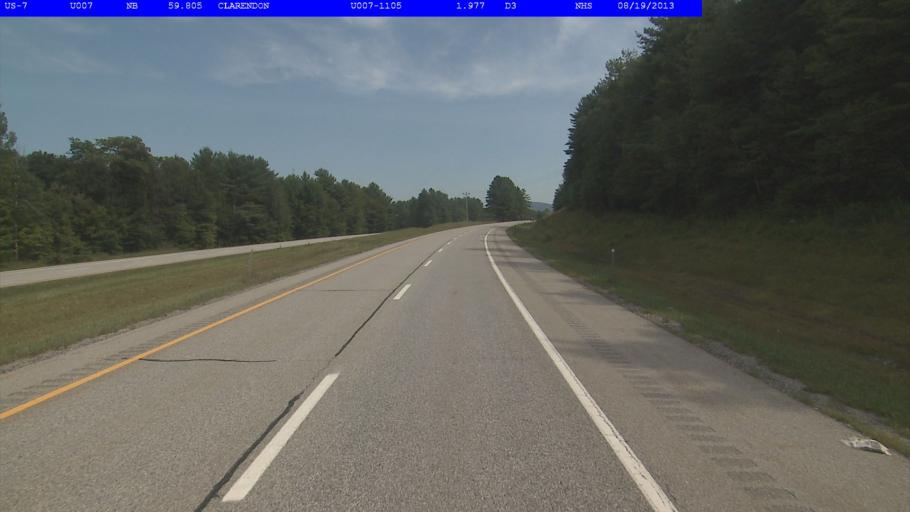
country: US
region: Vermont
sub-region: Rutland County
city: Rutland
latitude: 43.5232
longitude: -72.9666
